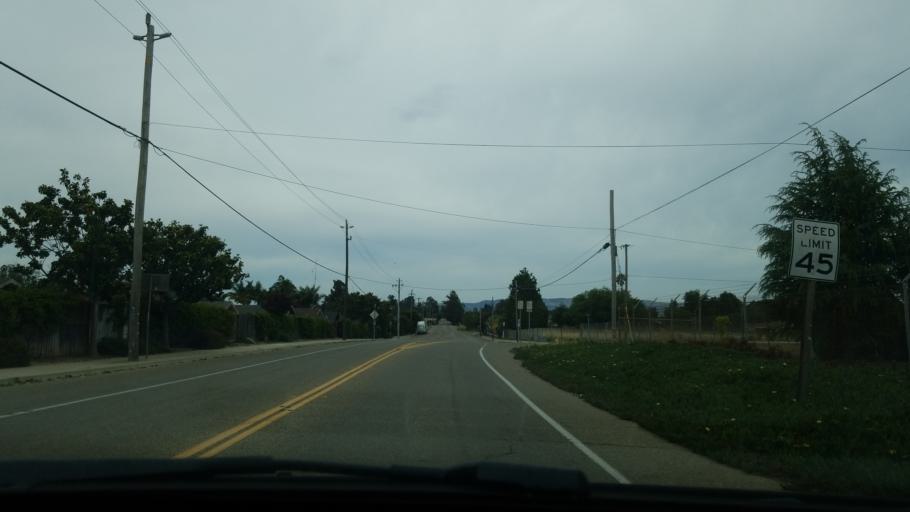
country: US
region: California
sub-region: San Luis Obispo County
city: Nipomo
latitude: 35.0214
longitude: -120.4891
